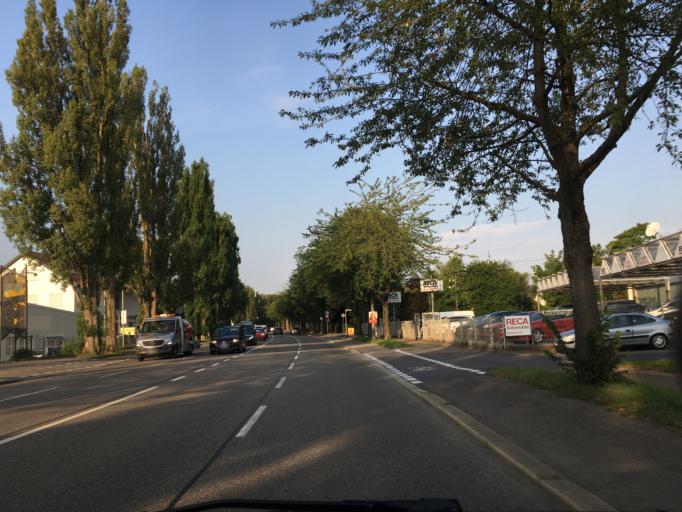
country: DE
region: Baden-Wuerttemberg
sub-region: Regierungsbezirk Stuttgart
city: Sindelfingen
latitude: 48.7064
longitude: 9.0165
